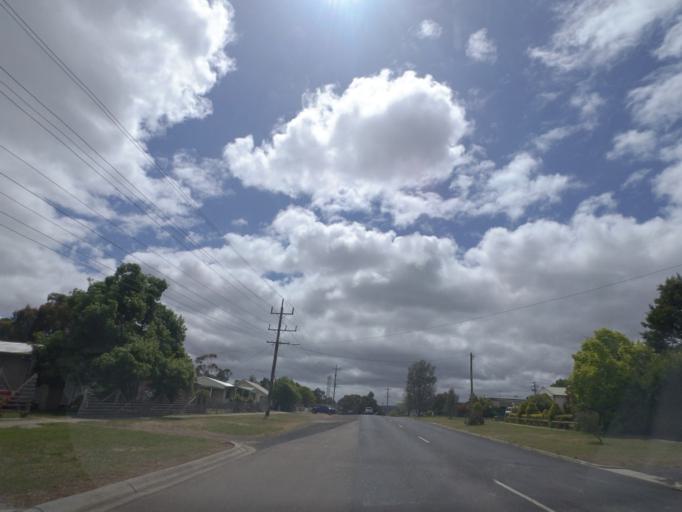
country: AU
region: Victoria
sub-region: Whittlesea
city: Whittlesea
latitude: -37.2072
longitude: 145.0451
